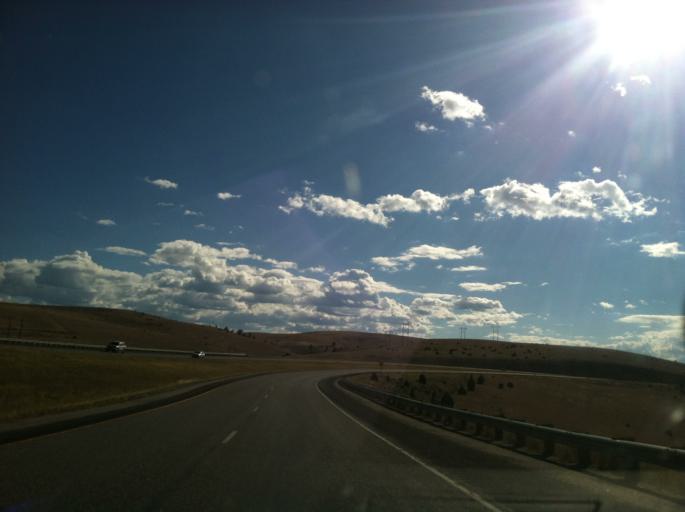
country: US
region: Montana
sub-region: Jefferson County
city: Whitehall
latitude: 45.8818
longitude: -111.8716
